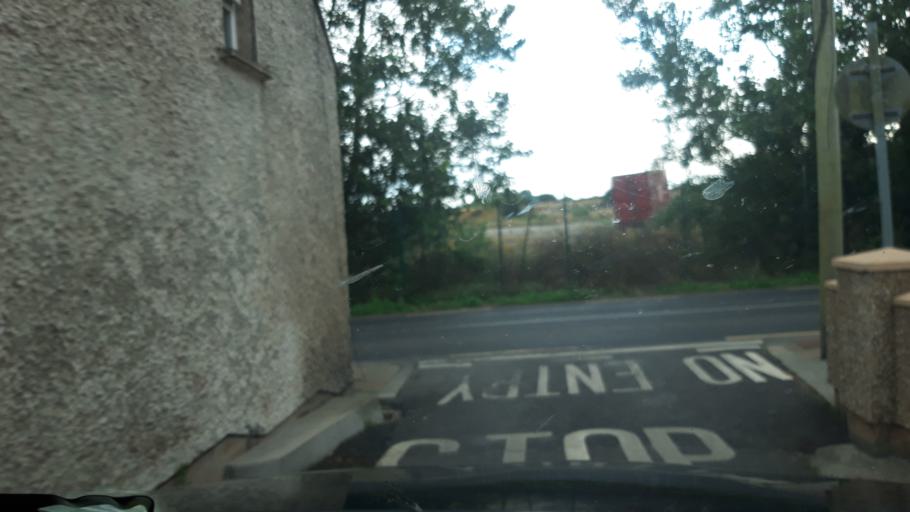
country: IE
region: Leinster
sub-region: Loch Garman
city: New Ross
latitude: 52.3942
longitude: -6.9546
